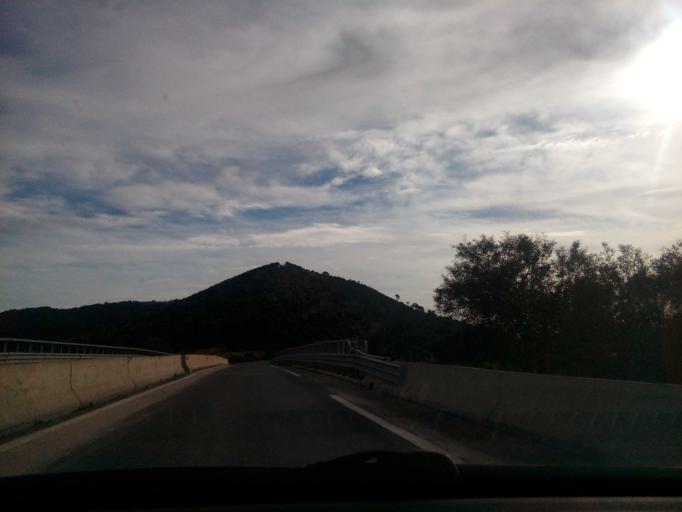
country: DZ
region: Sidi Bel Abbes
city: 'Ain el Berd
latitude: 35.3813
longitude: -0.5013
